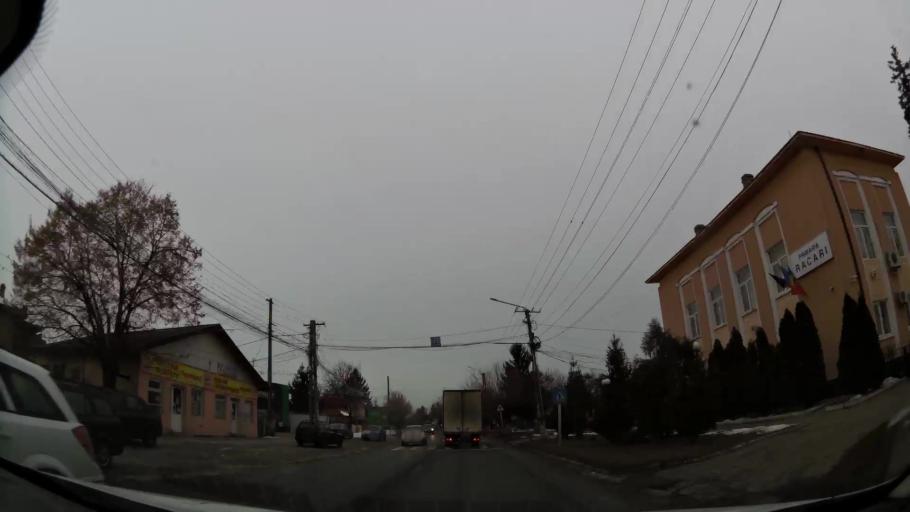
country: RO
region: Dambovita
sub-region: Comuna Racari
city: Racari
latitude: 44.6252
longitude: 25.7449
